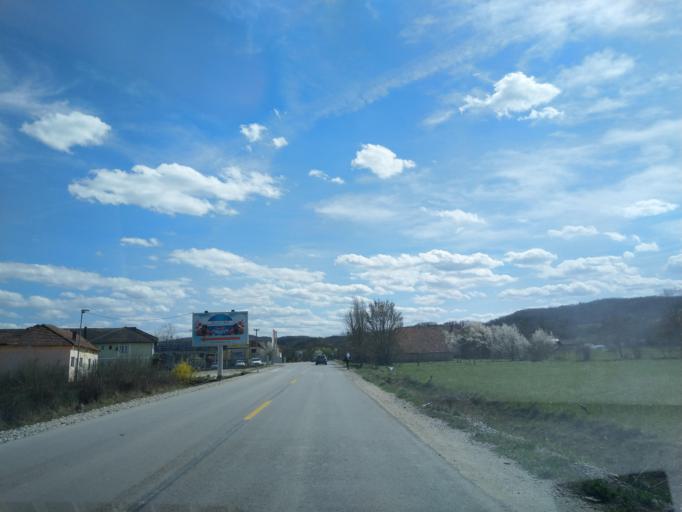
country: RS
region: Central Serbia
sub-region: Zlatiborski Okrug
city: Arilje
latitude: 43.7978
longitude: 20.0973
